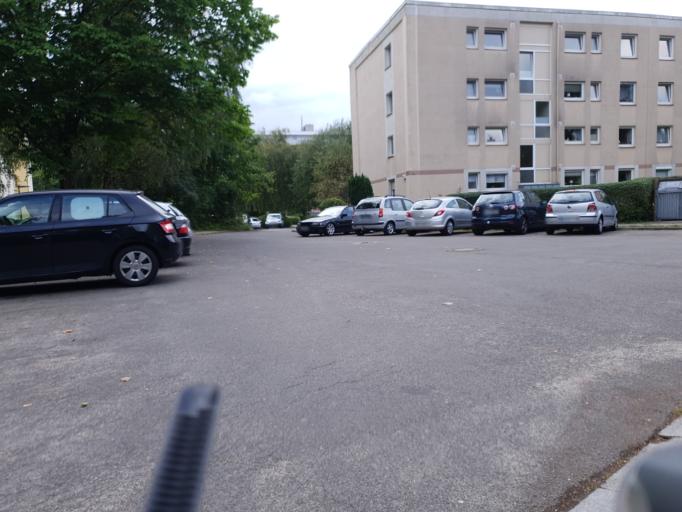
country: DE
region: Schleswig-Holstein
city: Kronshagen
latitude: 54.3581
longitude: 10.0817
